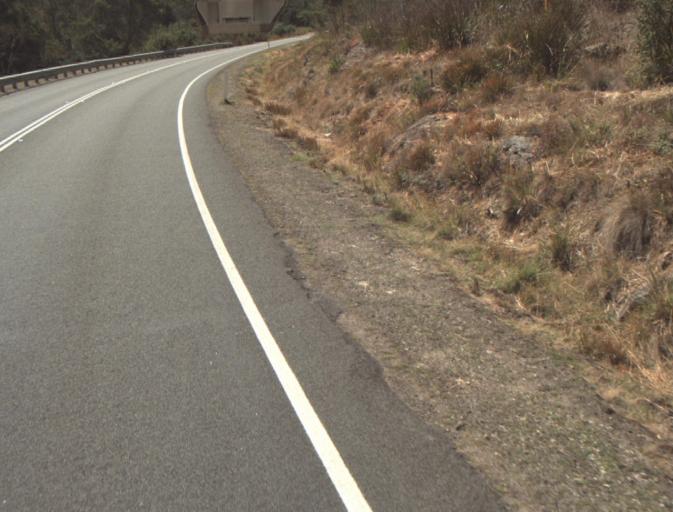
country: AU
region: Tasmania
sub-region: Launceston
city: Mayfield
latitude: -41.3564
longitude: 147.1422
